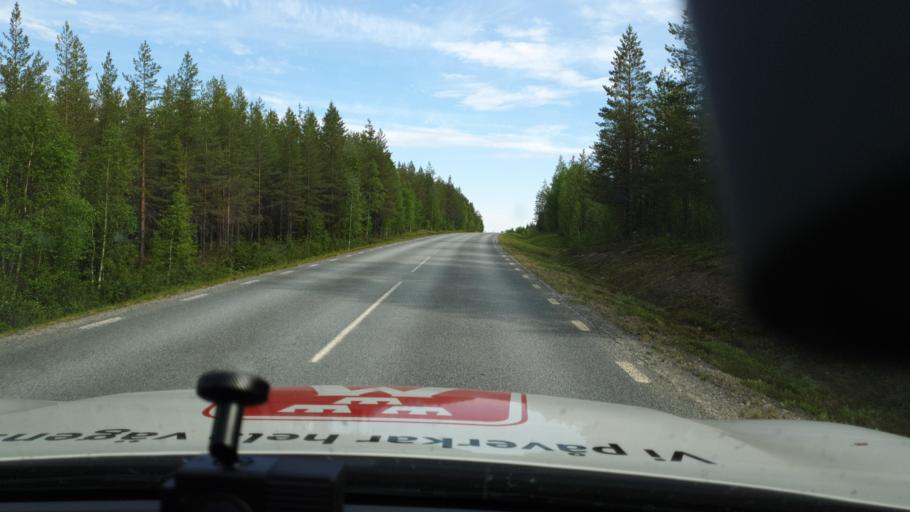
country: SE
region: Vaesterbotten
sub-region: Lycksele Kommun
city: Soderfors
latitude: 65.1634
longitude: 18.2557
